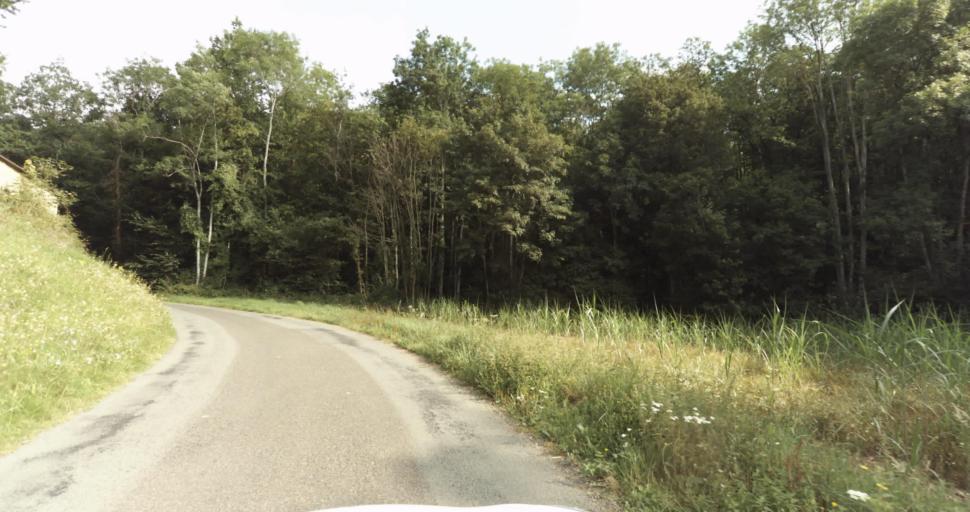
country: FR
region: Haute-Normandie
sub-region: Departement de l'Eure
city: Tillieres-sur-Avre
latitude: 48.7709
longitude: 1.1097
